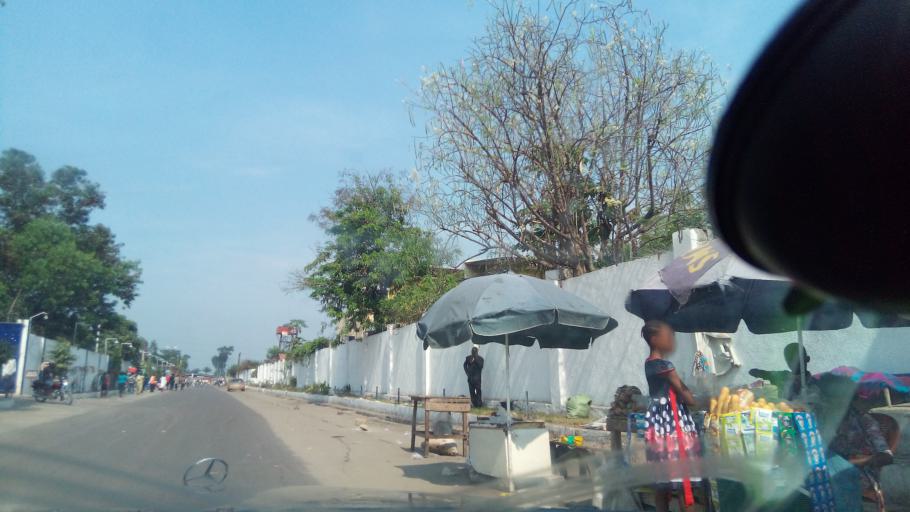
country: CD
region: Kinshasa
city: Masina
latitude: -4.3733
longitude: 15.3487
